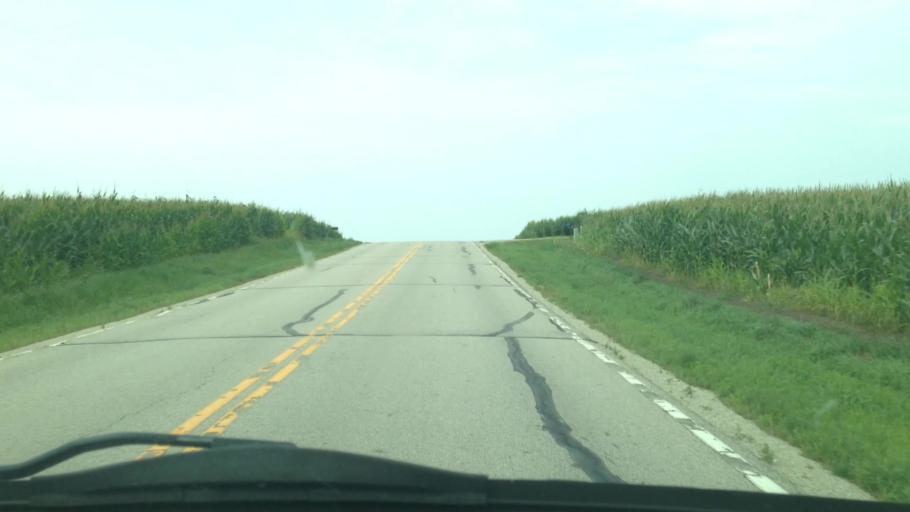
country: US
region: Minnesota
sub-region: Fillmore County
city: Preston
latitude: 43.7906
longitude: -91.9498
